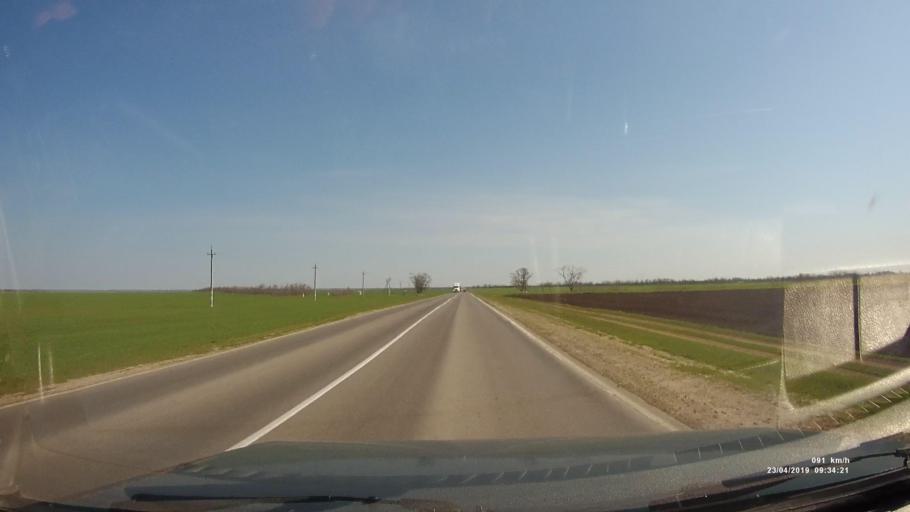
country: RU
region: Rostov
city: Gundorovskiy
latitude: 46.8108
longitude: 41.8578
